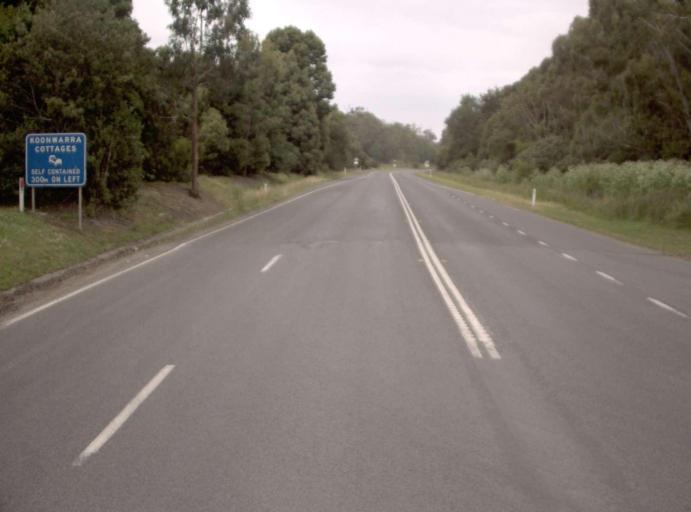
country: AU
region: Victoria
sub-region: Bass Coast
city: North Wonthaggi
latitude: -38.5355
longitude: 145.9503
